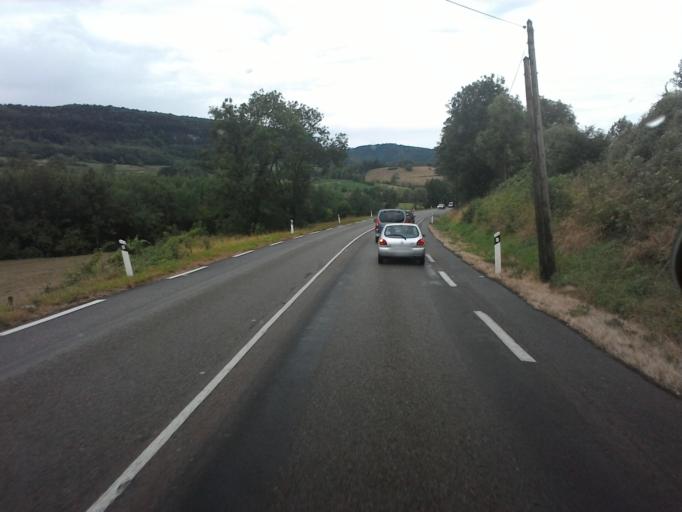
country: FR
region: Franche-Comte
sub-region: Departement du Jura
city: Poligny
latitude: 46.8563
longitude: 5.7125
